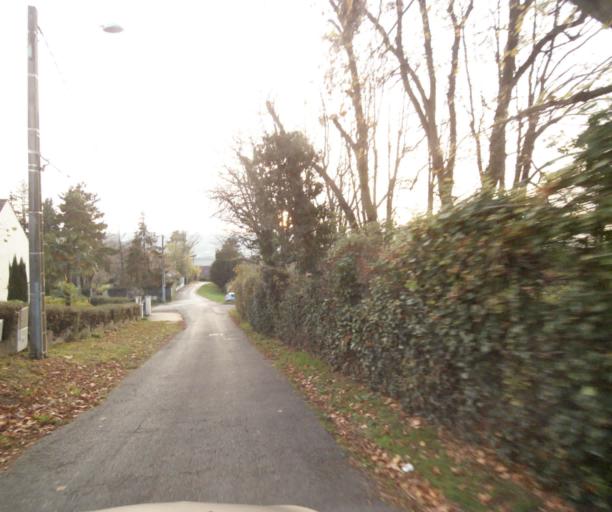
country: FR
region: Ile-de-France
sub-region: Departement des Yvelines
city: Triel-sur-Seine
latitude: 48.9827
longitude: 2.0114
